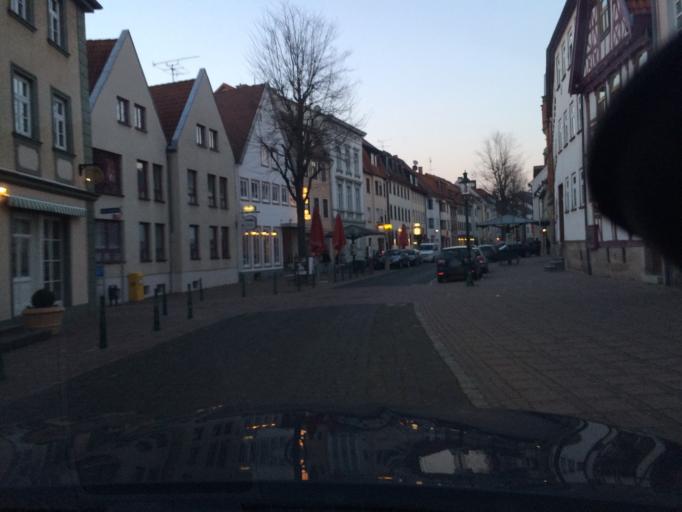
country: DE
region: Hesse
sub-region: Regierungsbezirk Kassel
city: Fulda
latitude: 50.5474
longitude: 9.6745
